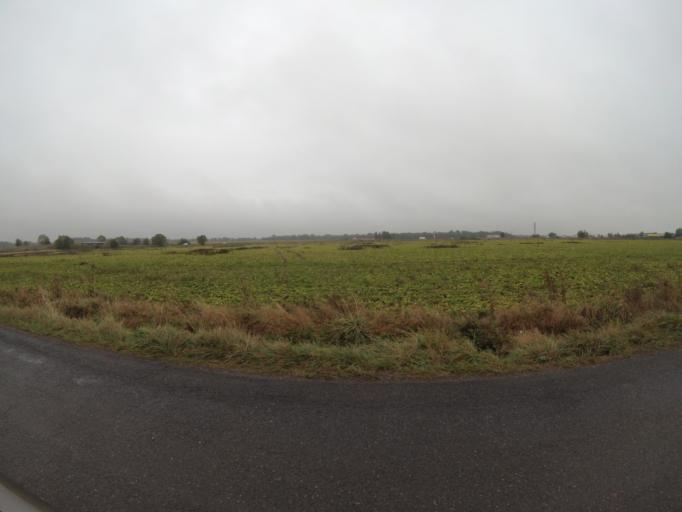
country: FR
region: Ile-de-France
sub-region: Departement de Seine-et-Marne
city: Chanteloup-en-Brie
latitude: 48.8328
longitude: 2.7521
